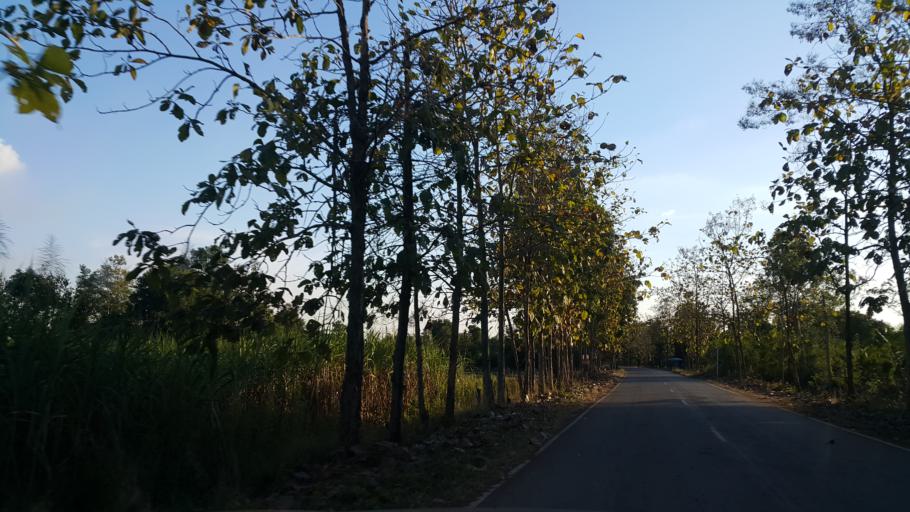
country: TH
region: Sukhothai
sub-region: Amphoe Si Satchanalai
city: Si Satchanalai
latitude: 17.5479
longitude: 99.9037
